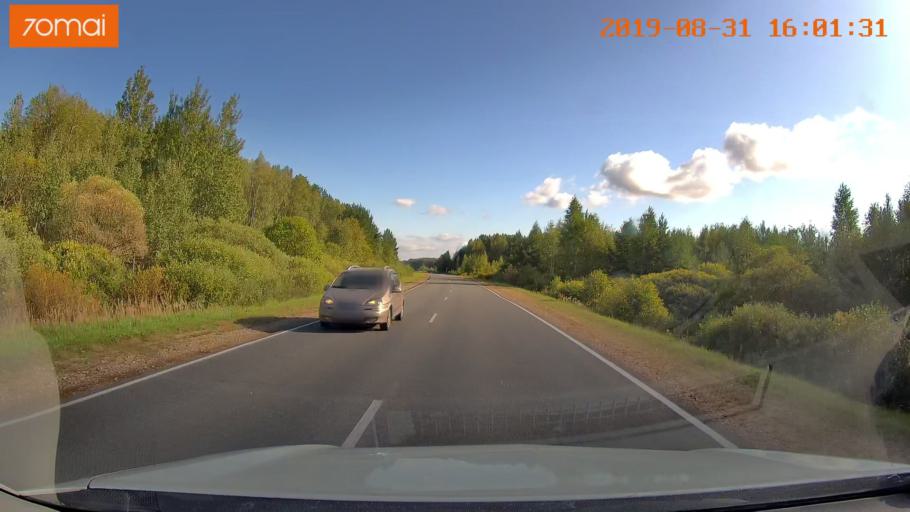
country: RU
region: Kaluga
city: Yukhnov
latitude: 54.6883
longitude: 35.2906
